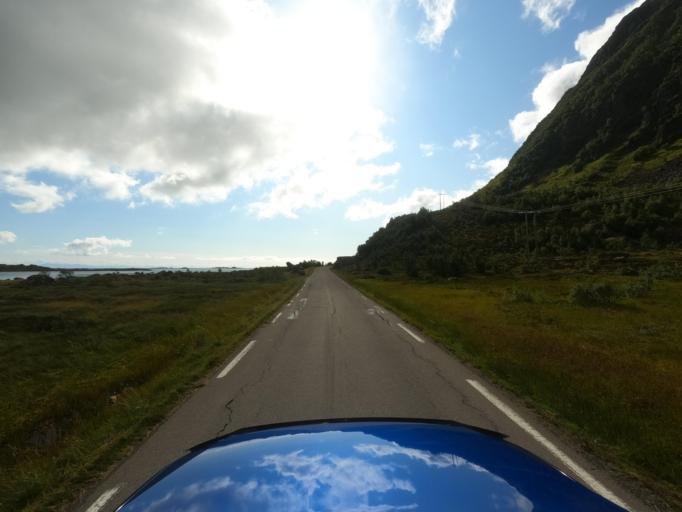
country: NO
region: Nordland
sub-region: Vestvagoy
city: Evjen
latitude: 68.1780
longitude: 13.8491
